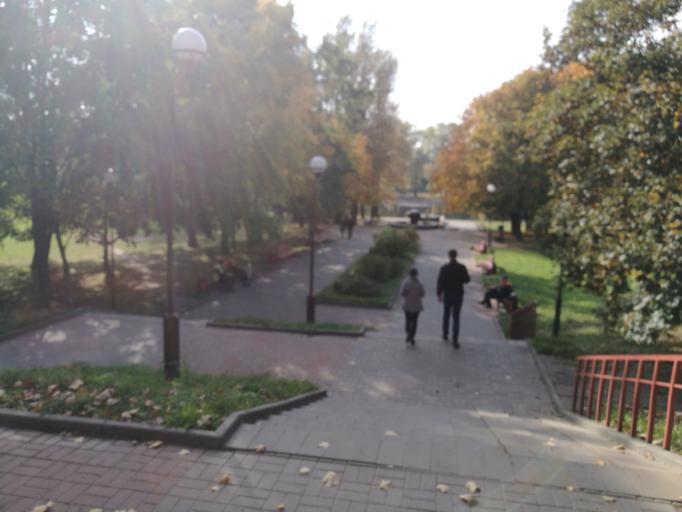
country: BY
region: Minsk
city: Minsk
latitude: 53.8975
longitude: 27.5179
